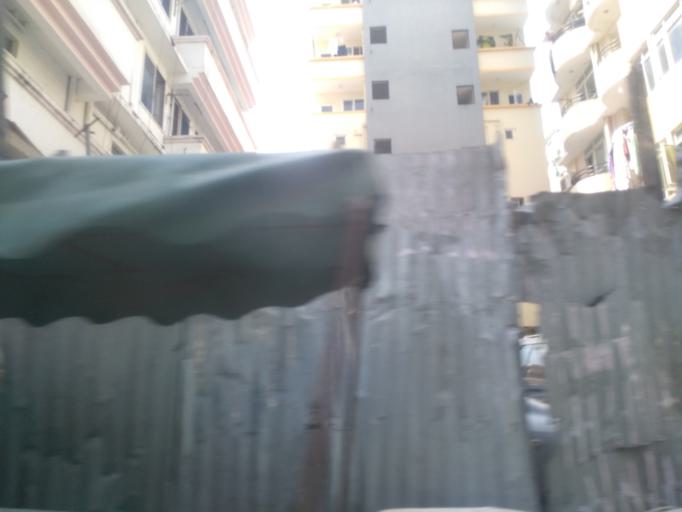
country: TZ
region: Dar es Salaam
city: Dar es Salaam
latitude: -6.8195
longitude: 39.2767
